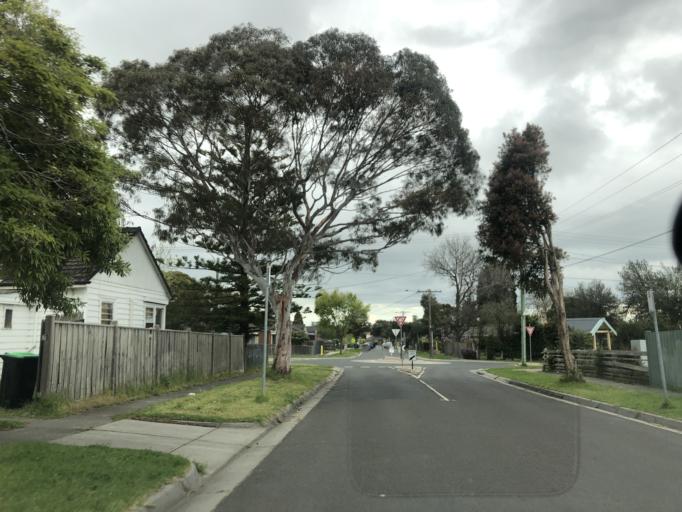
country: AU
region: Victoria
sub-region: Greater Dandenong
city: Dandenong
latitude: -37.9807
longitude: 145.2050
